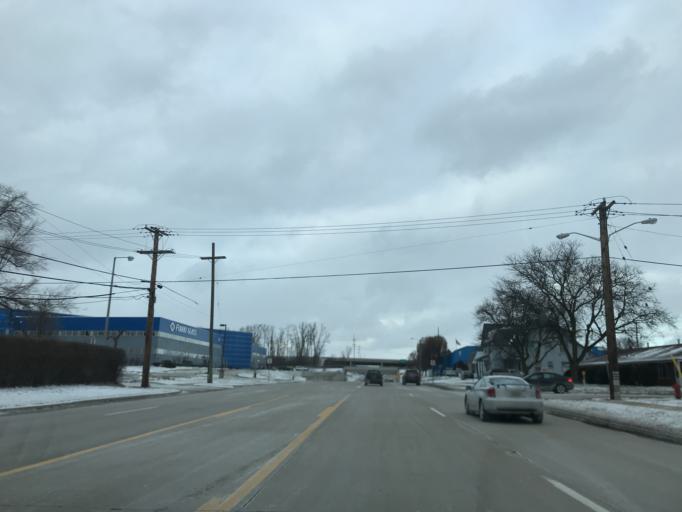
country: US
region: Michigan
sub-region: Wayne County
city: Plymouth
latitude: 42.3788
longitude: -83.4807
